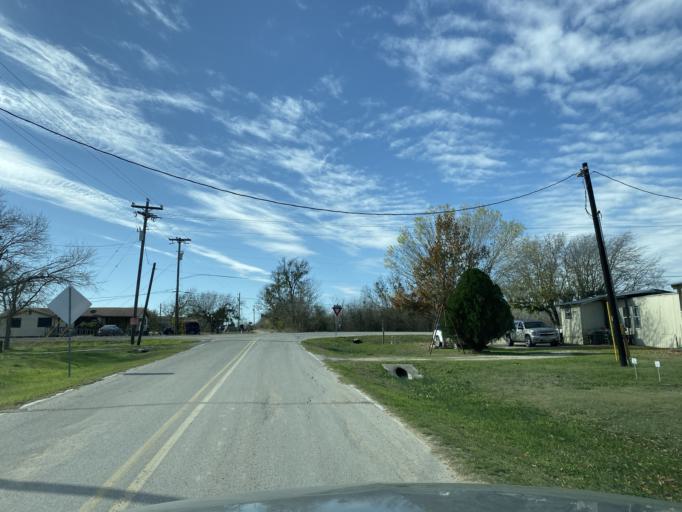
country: US
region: Texas
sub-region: Travis County
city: Onion Creek
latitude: 30.0845
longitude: -97.7024
